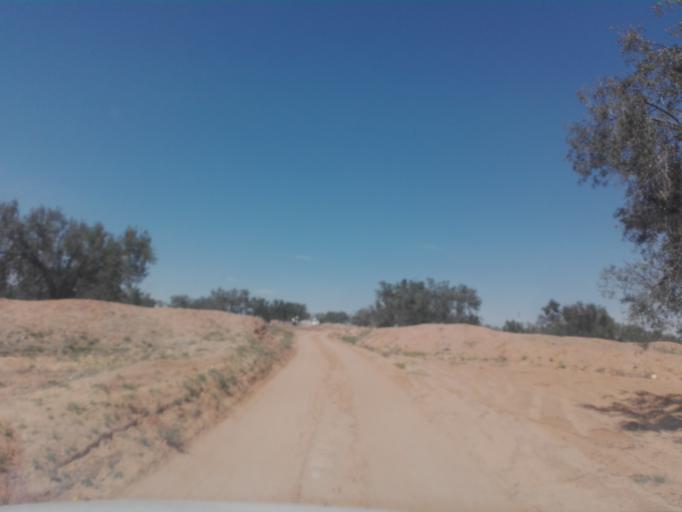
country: TN
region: Safaqis
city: Bi'r `Ali Bin Khalifah
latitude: 34.6630
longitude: 10.3120
